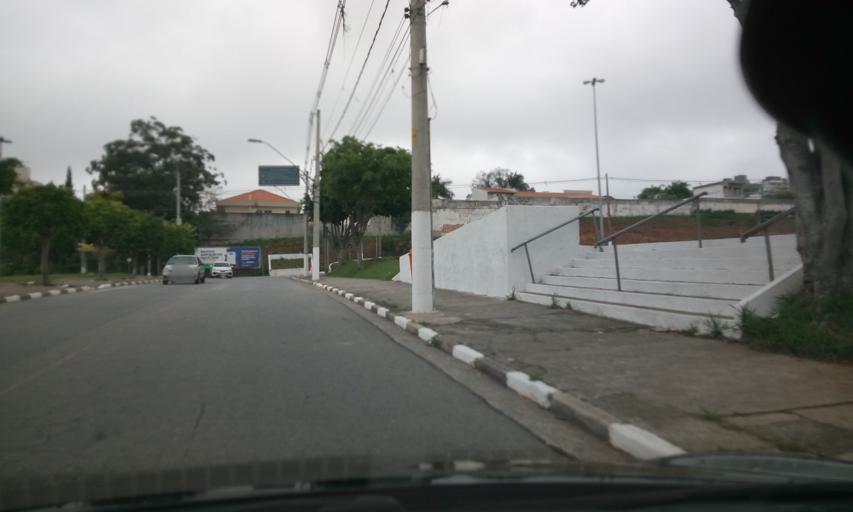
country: BR
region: Sao Paulo
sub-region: Sao Bernardo Do Campo
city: Sao Bernardo do Campo
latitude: -23.6783
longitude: -46.5597
